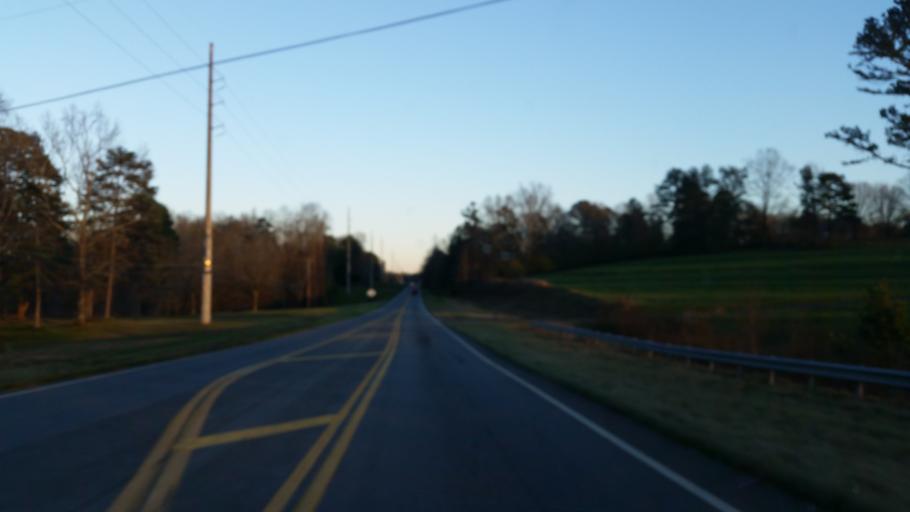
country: US
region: Georgia
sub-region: Hall County
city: Oakwood
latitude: 34.3107
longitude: -83.9918
